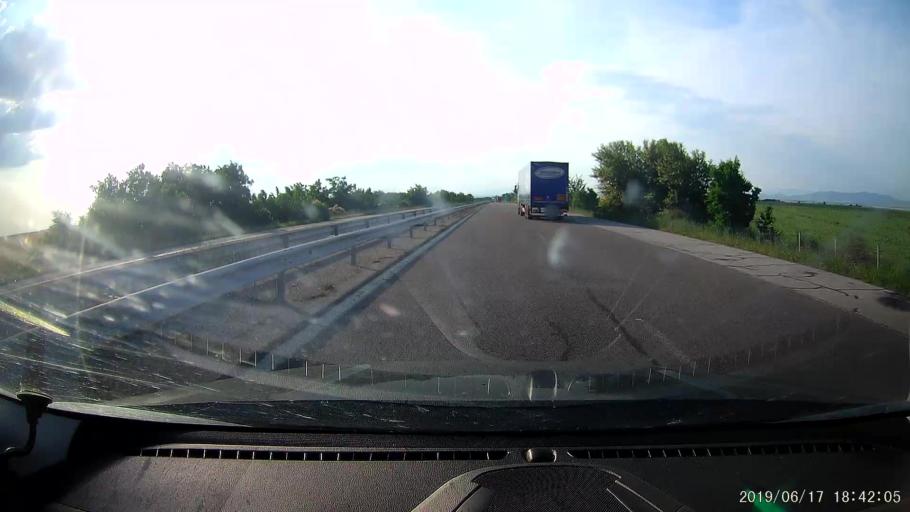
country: BG
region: Stara Zagora
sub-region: Obshtina Chirpan
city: Chirpan
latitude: 42.1848
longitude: 25.2435
